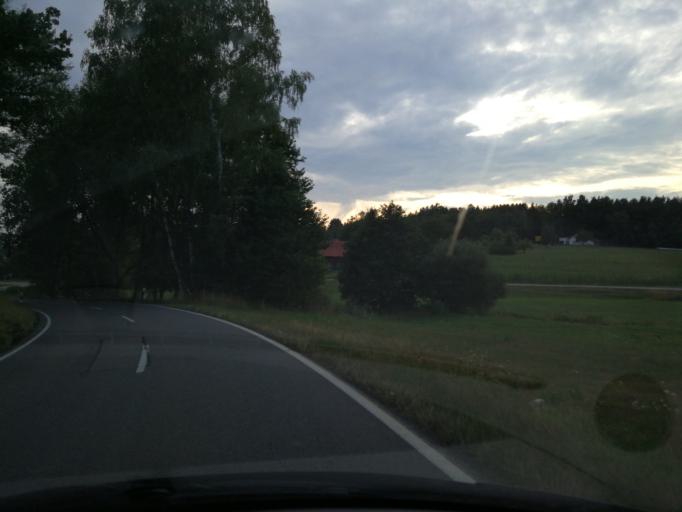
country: DE
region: Bavaria
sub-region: Lower Bavaria
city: Haibach
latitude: 49.0302
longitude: 12.7113
